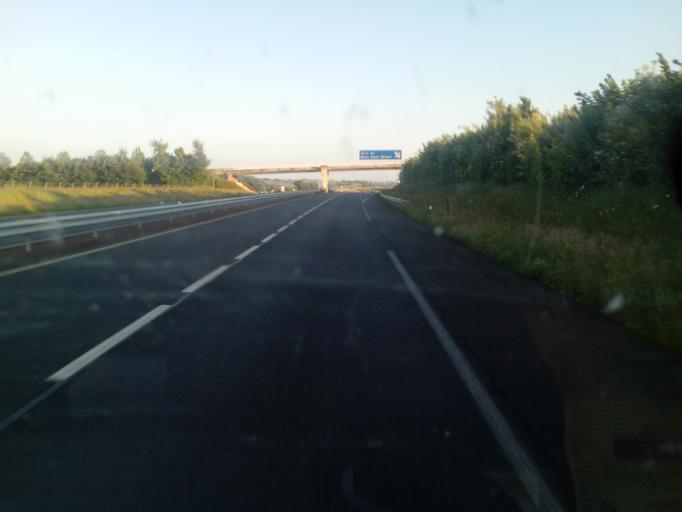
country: FR
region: Lower Normandy
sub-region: Departement de la Manche
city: Ducey
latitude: 48.5898
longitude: -1.3285
